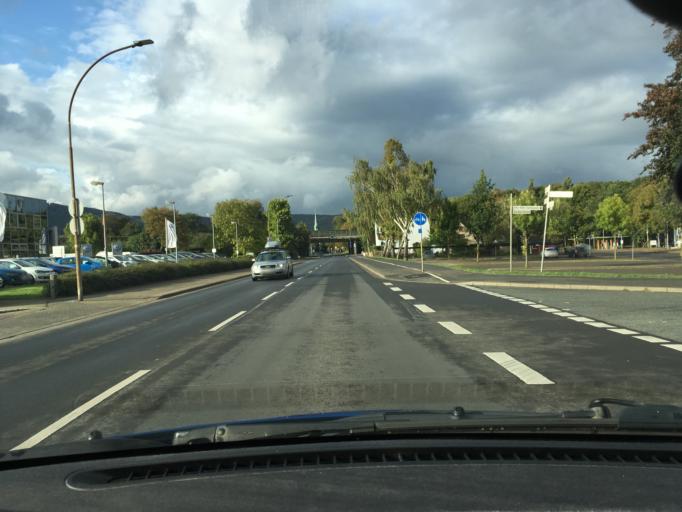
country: DE
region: Lower Saxony
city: Springe
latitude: 52.2020
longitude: 9.5567
